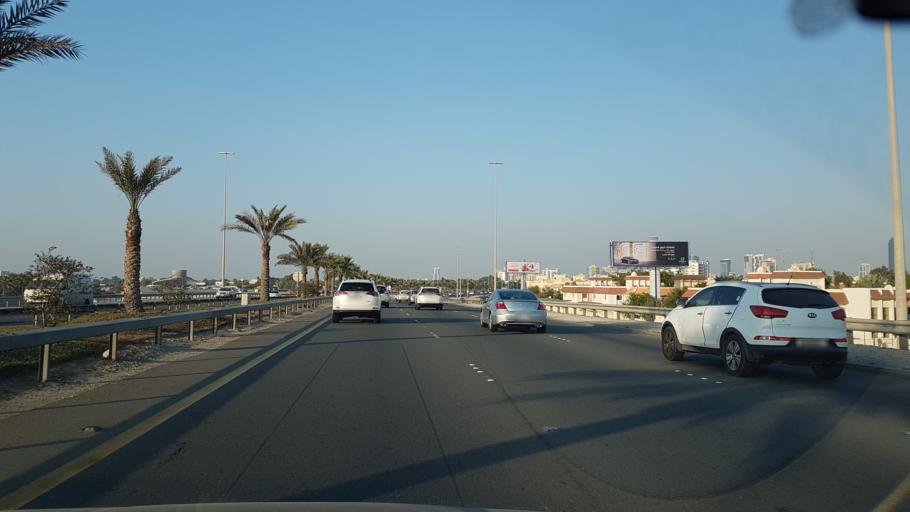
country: BH
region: Manama
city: Jidd Hafs
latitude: 26.2192
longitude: 50.5217
